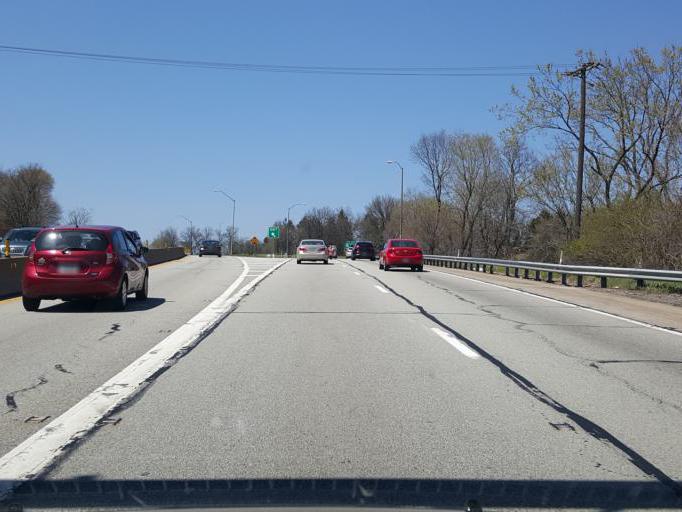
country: US
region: Pennsylvania
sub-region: Allegheny County
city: Churchill
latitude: 40.4442
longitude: -79.8411
